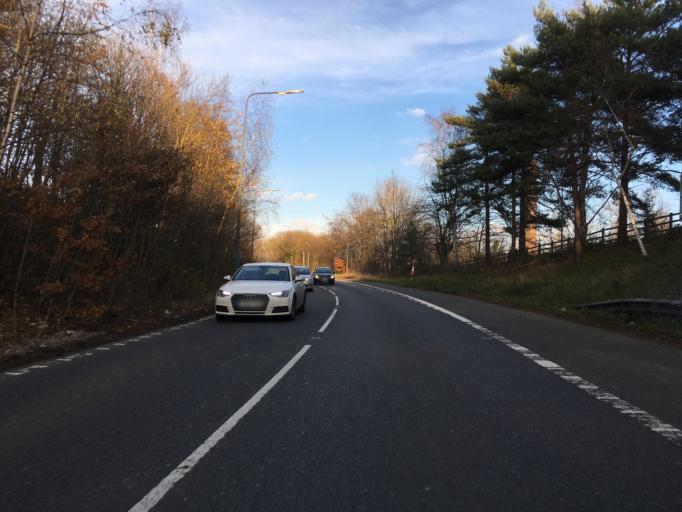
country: GB
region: England
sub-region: Manchester
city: Didsbury
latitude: 53.3967
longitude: -2.2218
